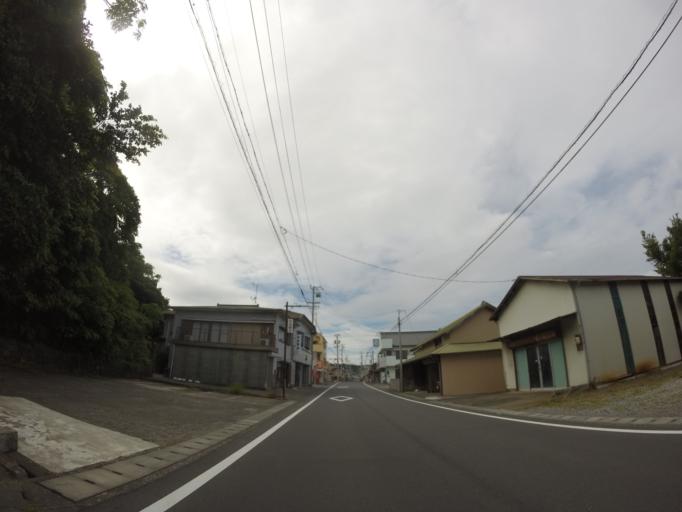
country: JP
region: Shizuoka
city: Oyama
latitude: 34.6308
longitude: 138.1958
